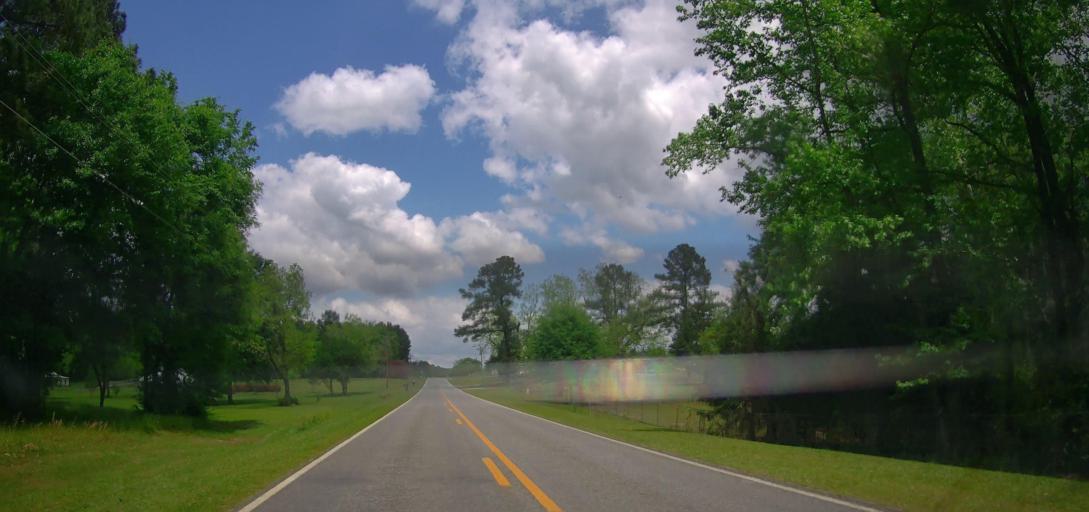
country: US
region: Georgia
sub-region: Laurens County
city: East Dublin
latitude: 32.5723
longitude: -82.7990
